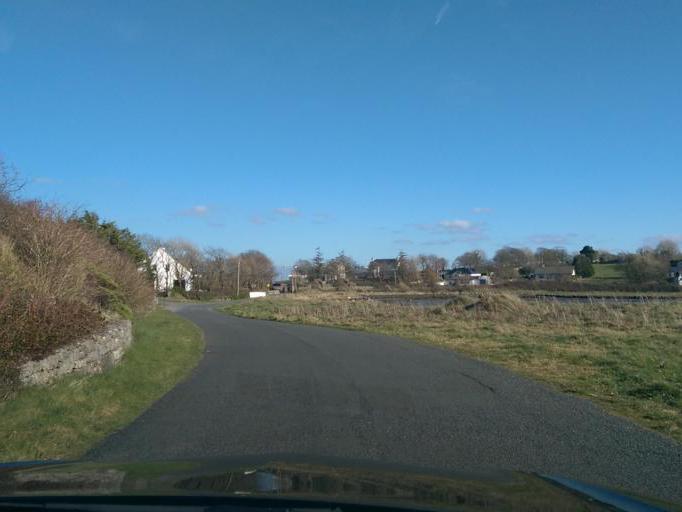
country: IE
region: Connaught
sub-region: County Galway
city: Oranmore
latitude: 53.2396
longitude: -8.9477
